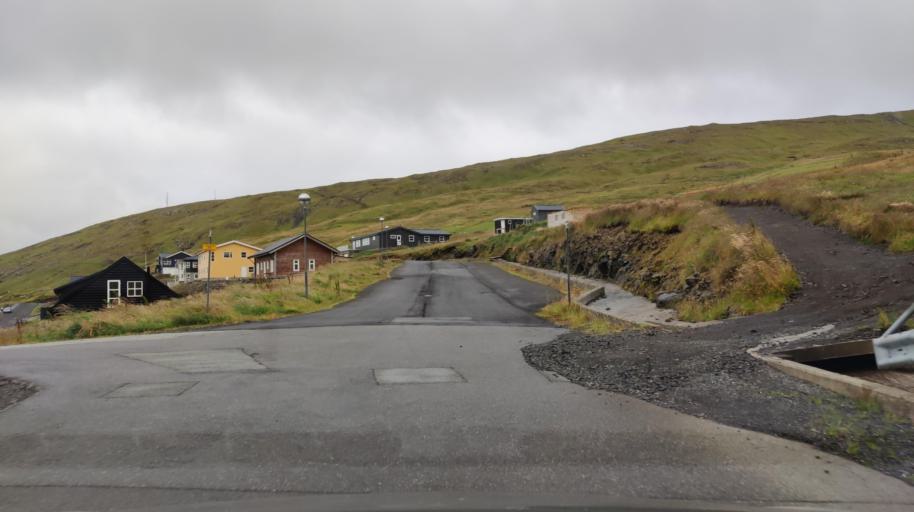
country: FO
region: Streymoy
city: Vestmanna
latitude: 62.1559
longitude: -7.1838
